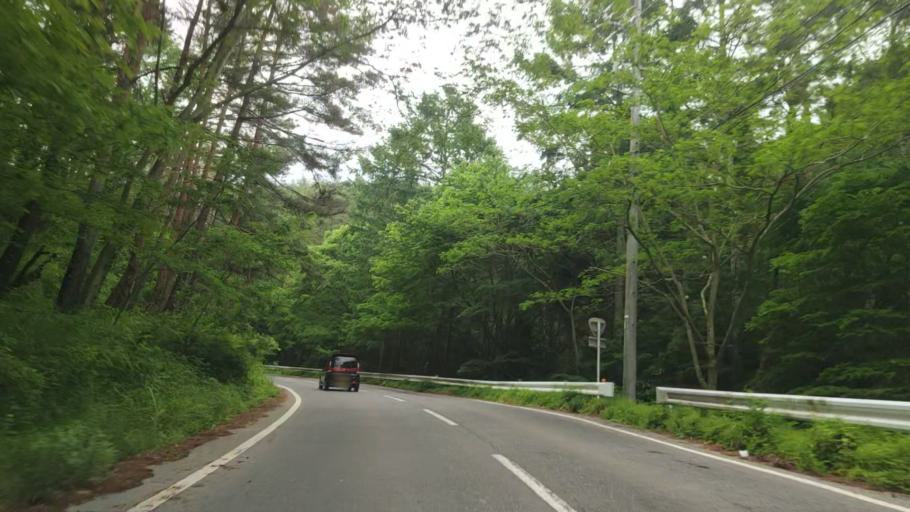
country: JP
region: Nagano
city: Kamimaruko
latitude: 36.2742
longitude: 138.2718
